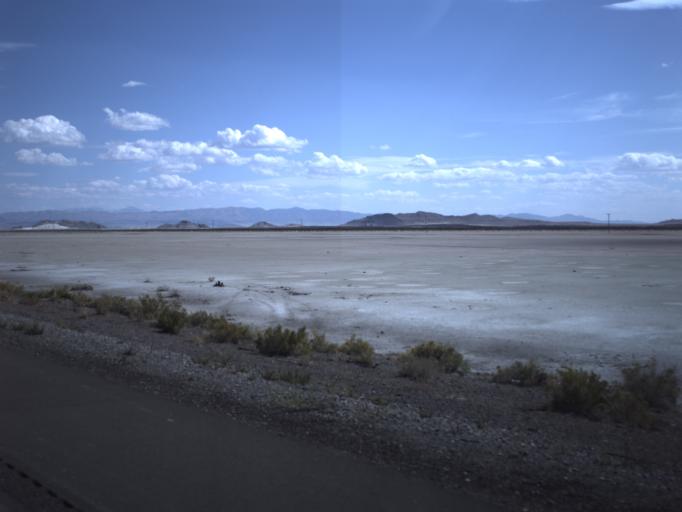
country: US
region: Utah
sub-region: Tooele County
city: Wendover
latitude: 40.7279
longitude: -113.3654
